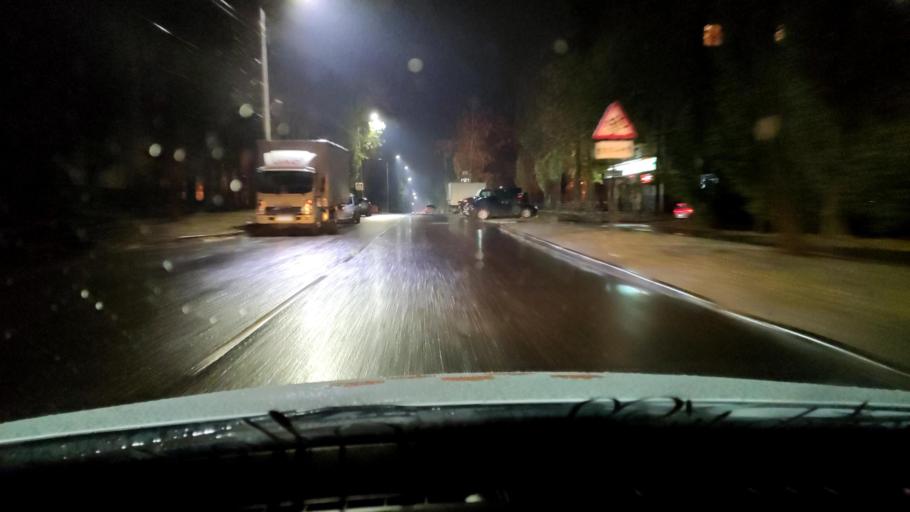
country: RU
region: Voronezj
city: Voronezh
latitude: 51.6502
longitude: 39.1280
